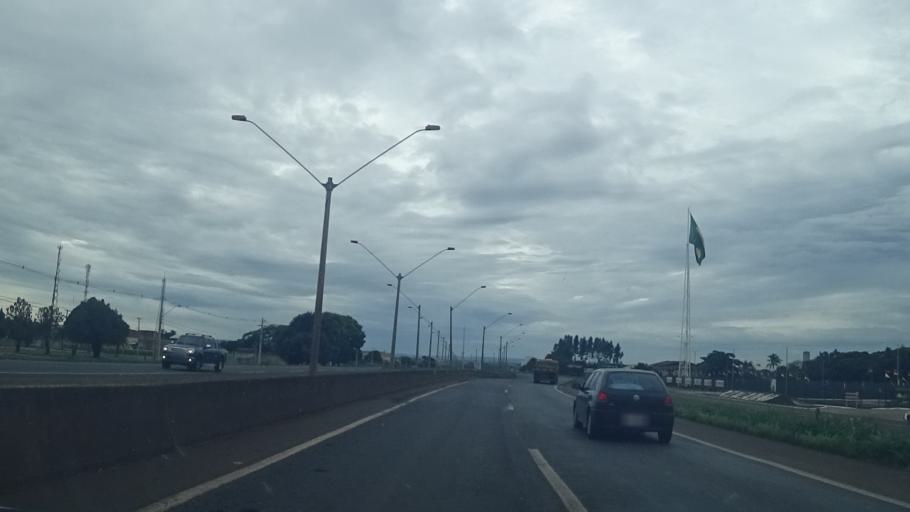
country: BR
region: Goias
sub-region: Itumbiara
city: Itumbiara
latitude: -18.3914
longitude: -49.2059
